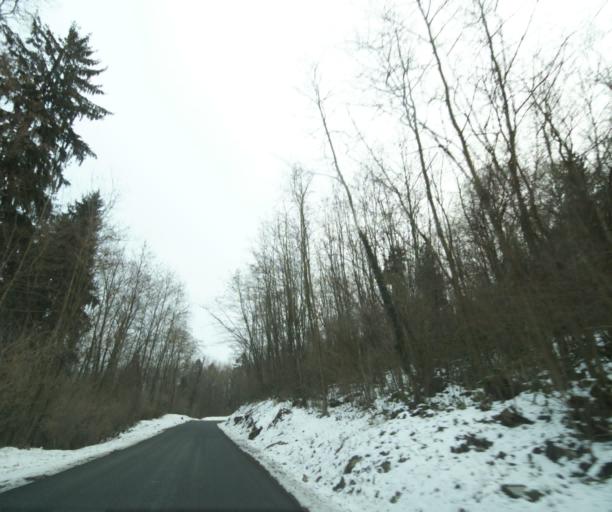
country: FR
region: Rhone-Alpes
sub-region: Departement de la Haute-Savoie
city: Arthaz-Pont-Notre-Dame
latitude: 46.1546
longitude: 6.2389
